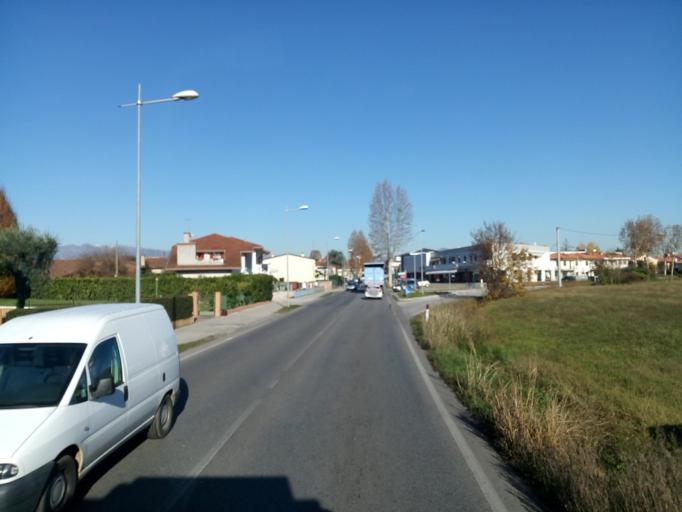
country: IT
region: Veneto
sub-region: Provincia di Treviso
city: Valla
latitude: 45.7026
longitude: 11.9295
